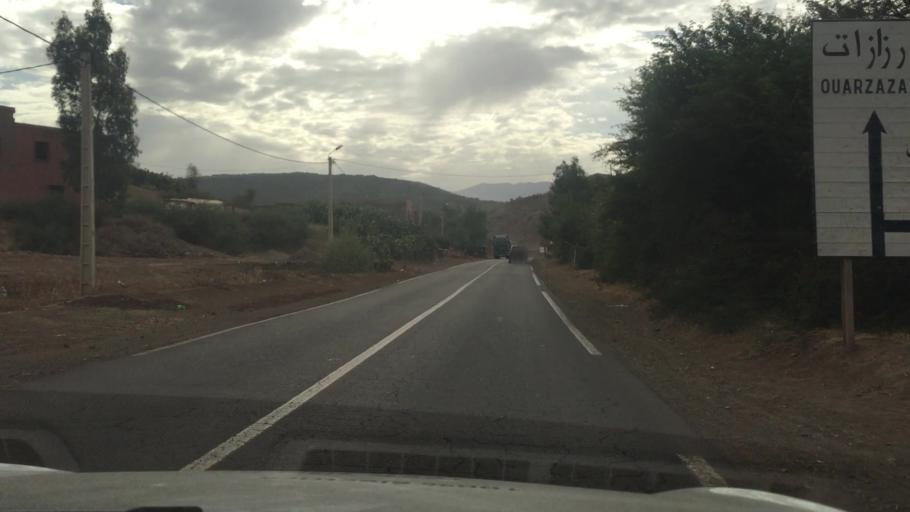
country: MA
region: Marrakech-Tensift-Al Haouz
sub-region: Al-Haouz
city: Touama
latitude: 31.5478
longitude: -7.5748
